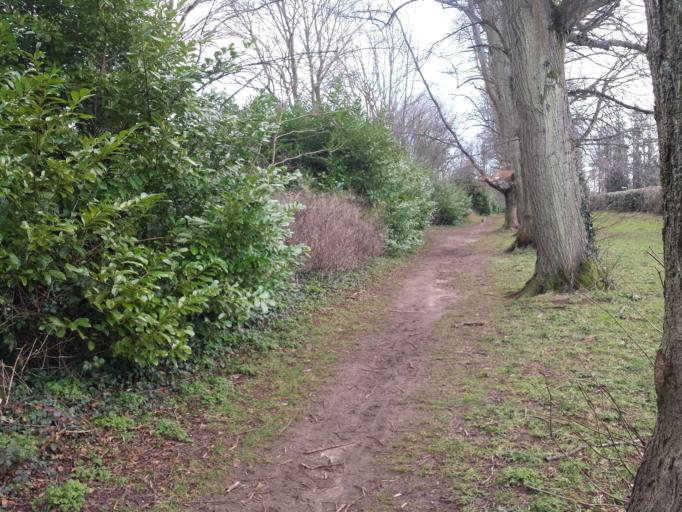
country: GB
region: England
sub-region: Surrey
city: Godalming
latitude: 51.1760
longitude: -0.6079
